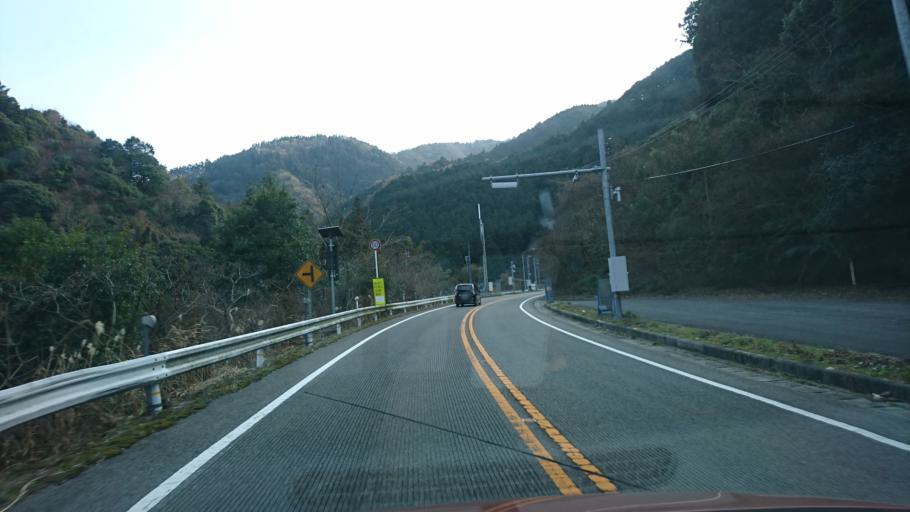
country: JP
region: Ehime
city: Hojo
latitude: 33.9555
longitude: 132.9118
